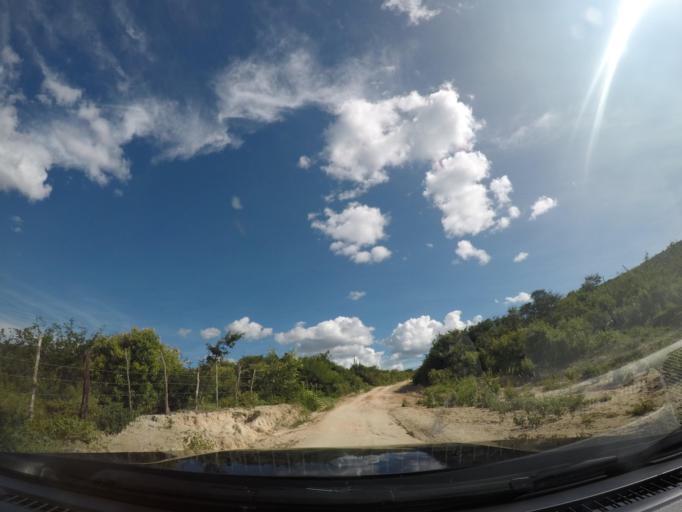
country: BR
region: Bahia
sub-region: Barra Da Estiva
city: Barra da Estiva
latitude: -13.1987
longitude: -41.5949
